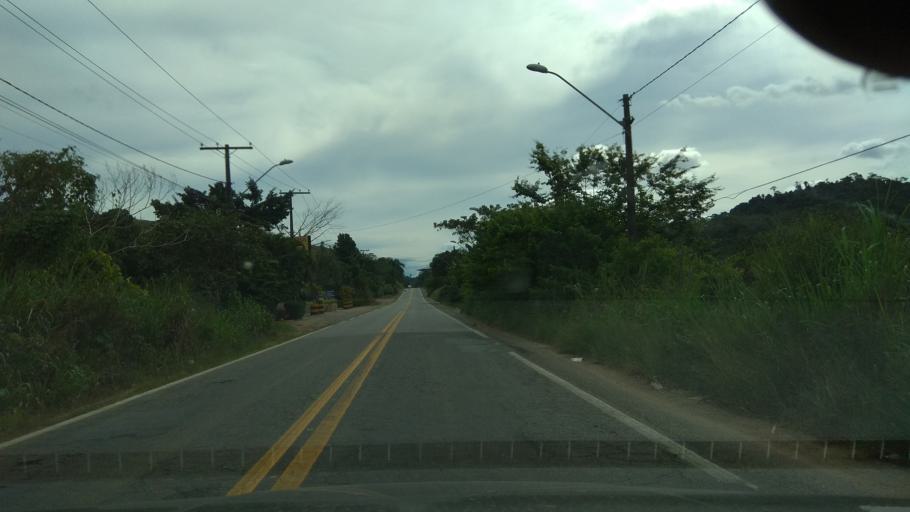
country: BR
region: Bahia
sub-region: Ubata
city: Ubata
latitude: -14.1975
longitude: -39.5404
